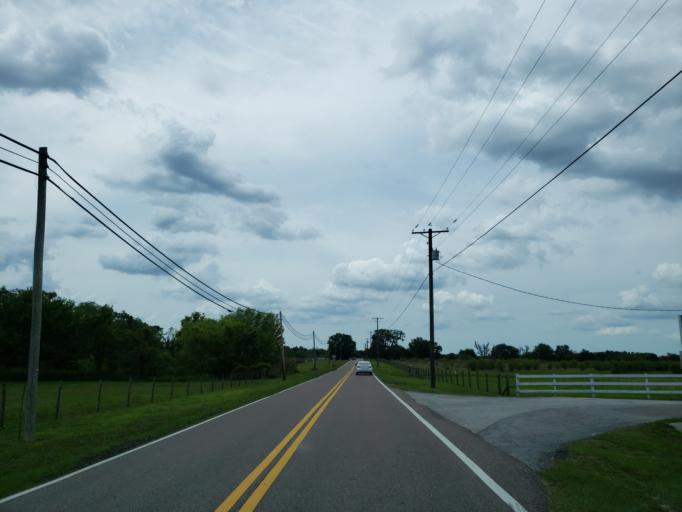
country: US
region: Florida
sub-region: Hillsborough County
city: Keystone
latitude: 28.1150
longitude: -82.6058
